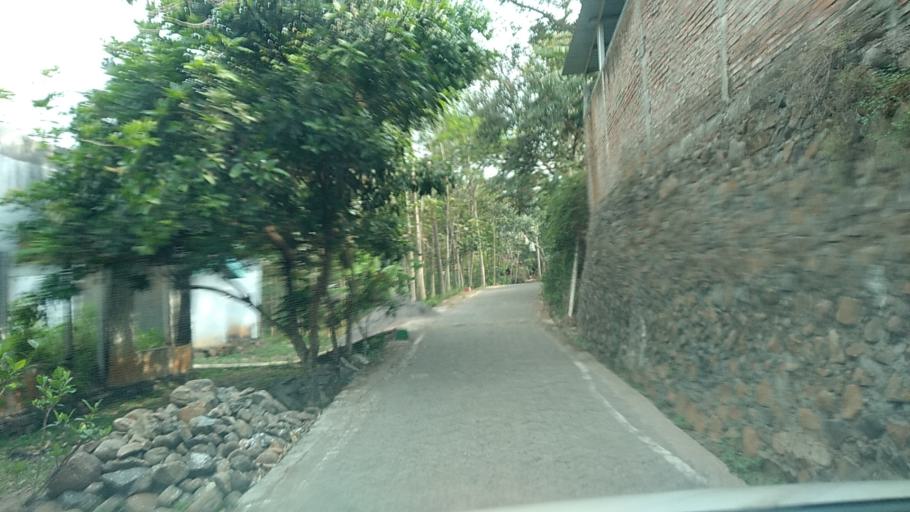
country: ID
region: Central Java
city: Ungaran
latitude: -7.1116
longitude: 110.3871
